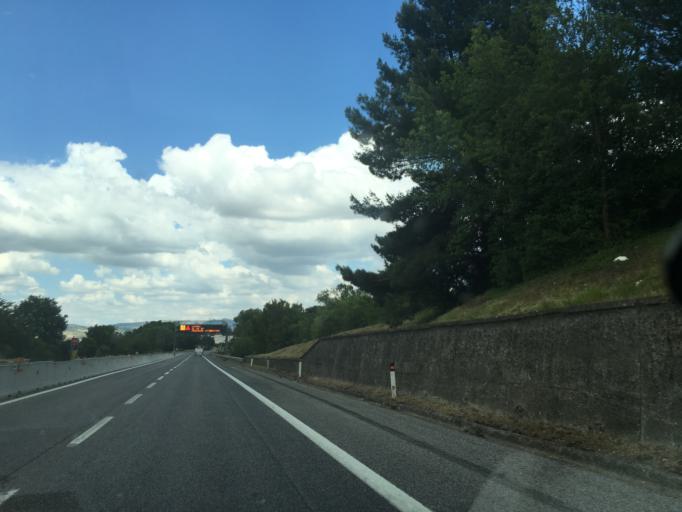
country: IT
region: Campania
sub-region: Provincia di Avellino
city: Grottaminarda
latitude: 41.0608
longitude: 15.0492
